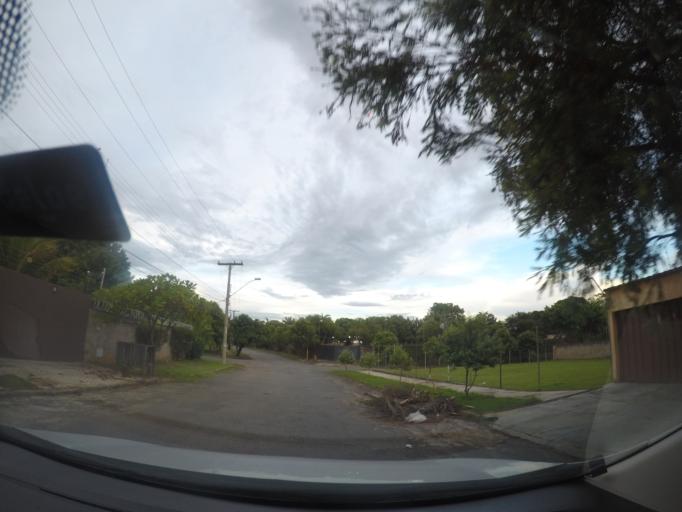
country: BR
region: Goias
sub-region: Goiania
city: Goiania
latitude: -16.6517
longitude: -49.2243
